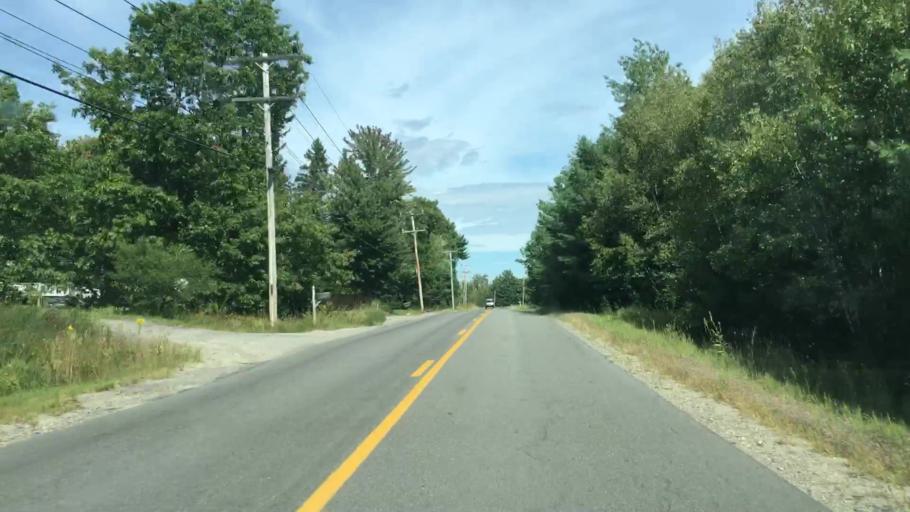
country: US
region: Maine
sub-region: Penobscot County
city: Lincoln
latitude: 45.4321
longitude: -68.4674
